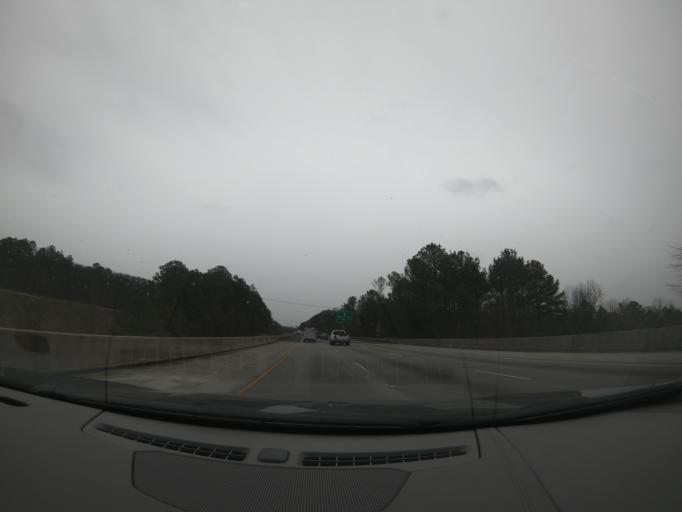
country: US
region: Georgia
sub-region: Catoosa County
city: Indian Springs
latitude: 34.9408
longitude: -85.1676
